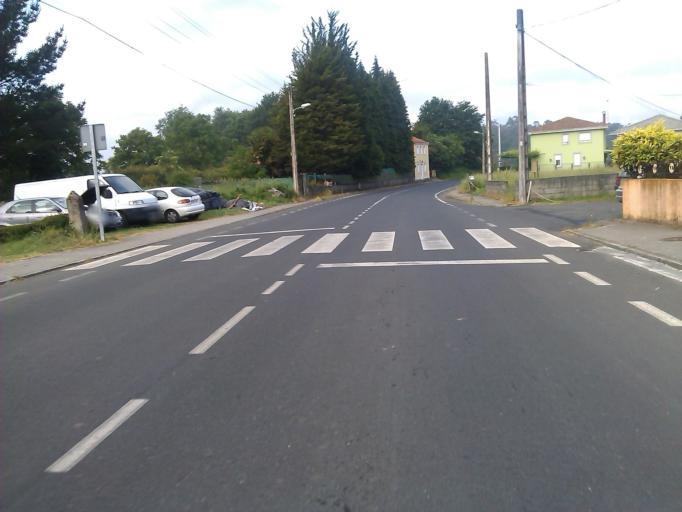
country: ES
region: Galicia
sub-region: Provincia da Coruna
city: Melide
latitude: 42.9096
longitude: -8.0269
